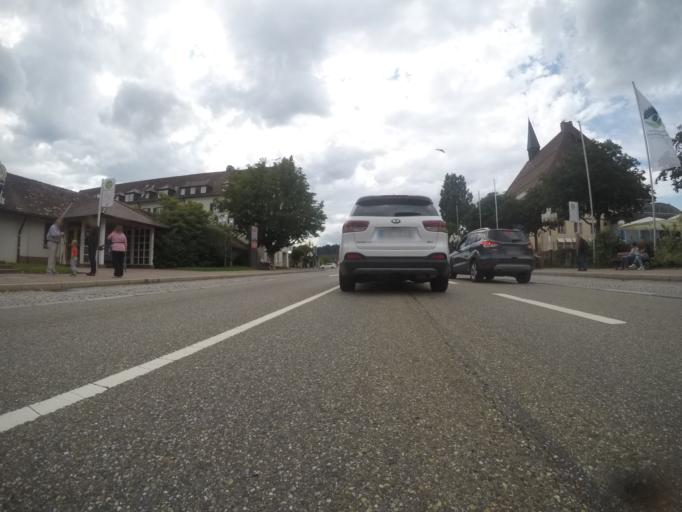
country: DE
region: Baden-Wuerttemberg
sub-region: Karlsruhe Region
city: Freudenstadt
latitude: 48.4641
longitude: 8.4122
